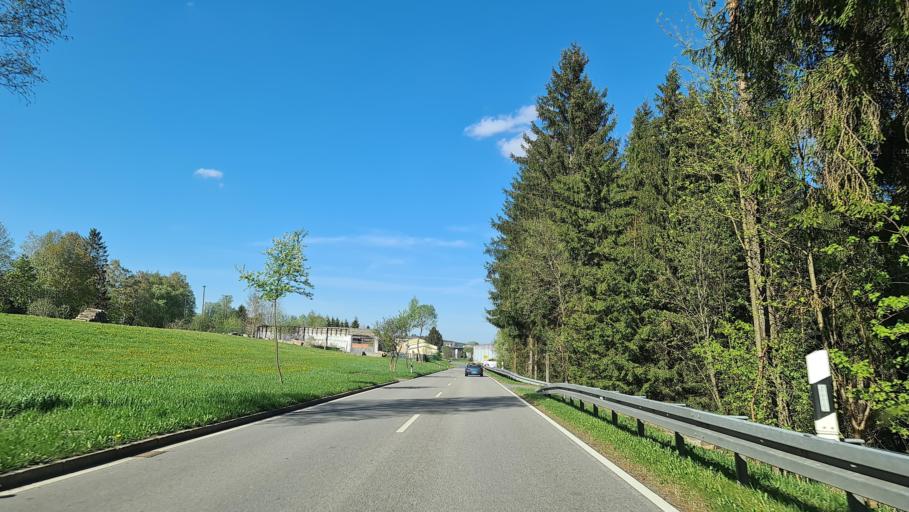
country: DE
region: Saxony
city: Hammerbrucke
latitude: 50.4329
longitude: 12.4063
